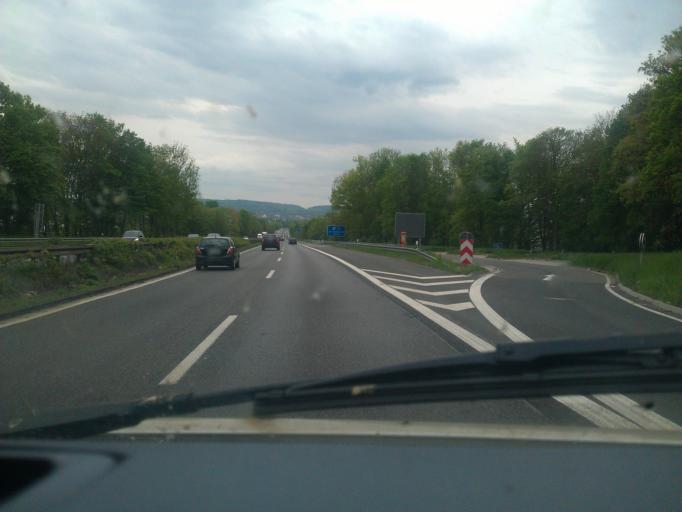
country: DE
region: North Rhine-Westphalia
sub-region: Regierungsbezirk Koln
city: Wurselen
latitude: 50.7965
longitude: 6.1415
